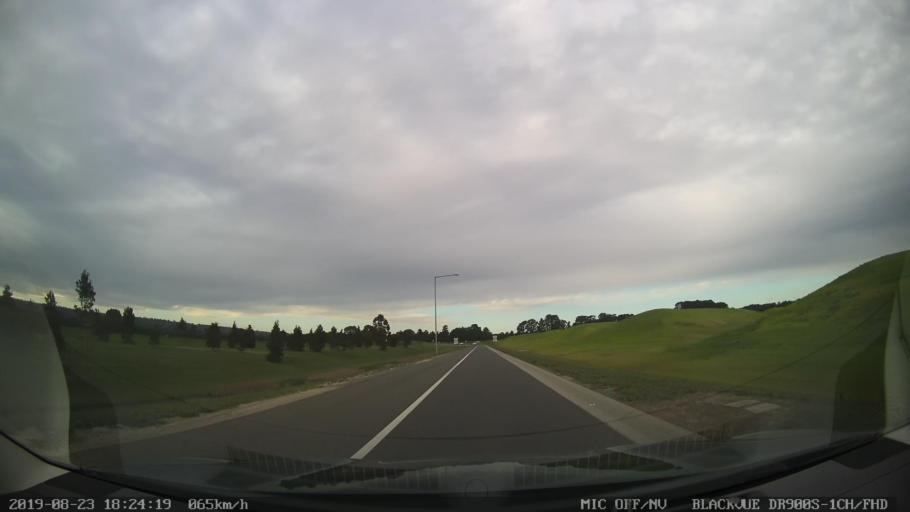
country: AU
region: Victoria
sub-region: Mornington Peninsula
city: Moorooduc
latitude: -38.2320
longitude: 145.1234
